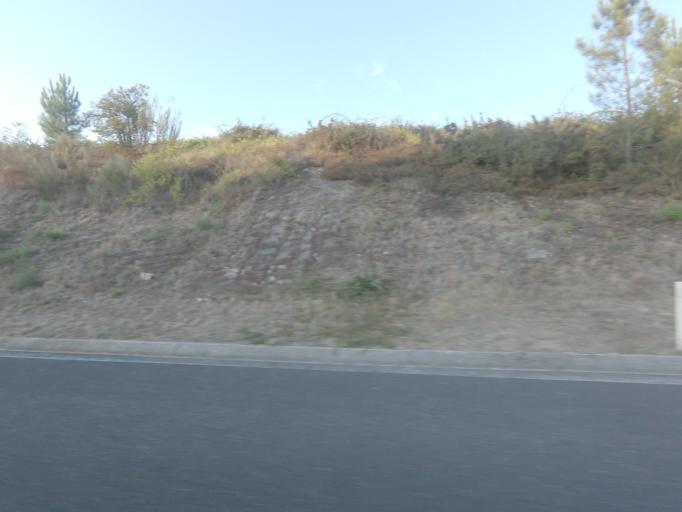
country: PT
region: Leiria
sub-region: Leiria
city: Santa Catarina da Serra
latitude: 39.7041
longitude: -8.7034
